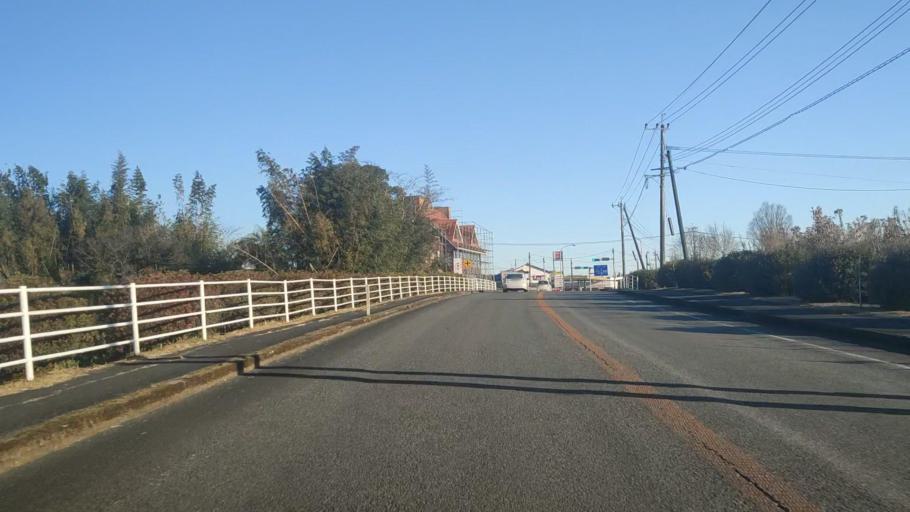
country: JP
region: Miyazaki
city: Takanabe
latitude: 32.1945
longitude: 131.5246
